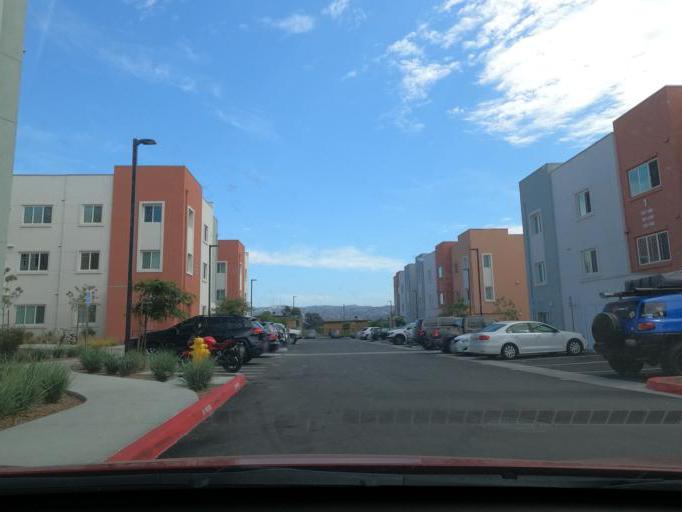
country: MX
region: Baja California
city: Tijuana
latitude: 32.5566
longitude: -117.0457
